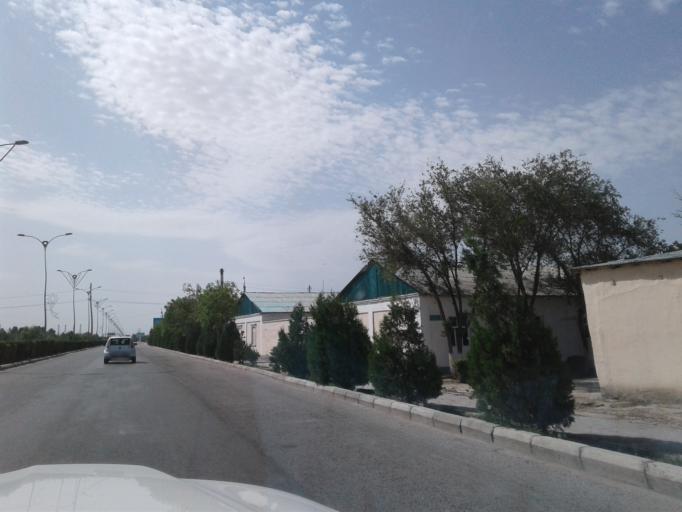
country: TM
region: Dasoguz
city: Dasoguz
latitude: 41.8318
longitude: 59.9399
